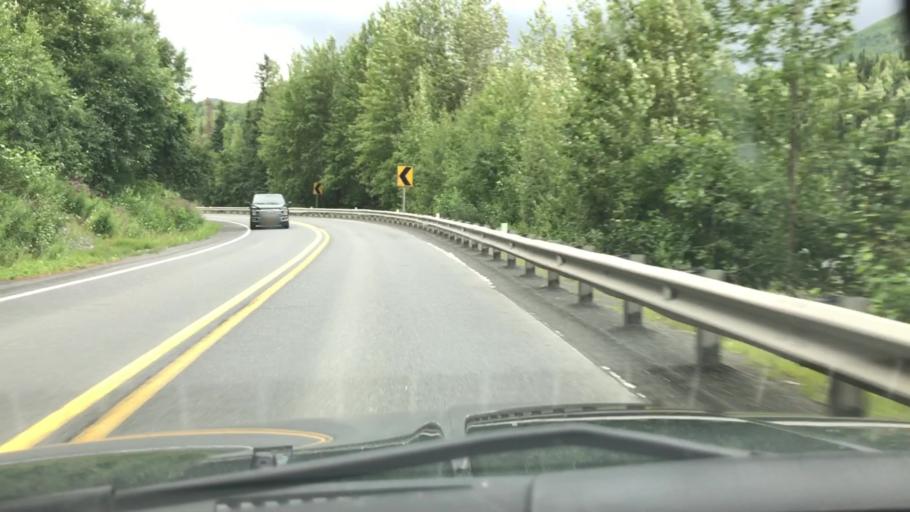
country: US
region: Alaska
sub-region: Kenai Peninsula Borough
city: Seward
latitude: 60.4860
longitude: -149.8563
